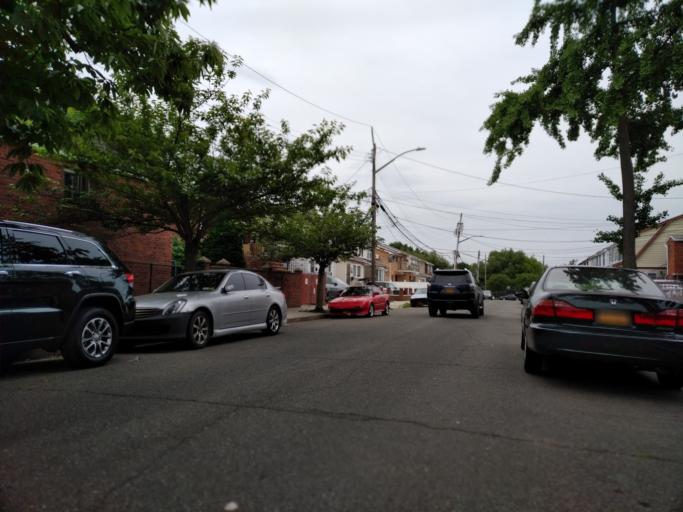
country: US
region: New York
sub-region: Queens County
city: Jamaica
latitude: 40.7459
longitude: -73.8154
